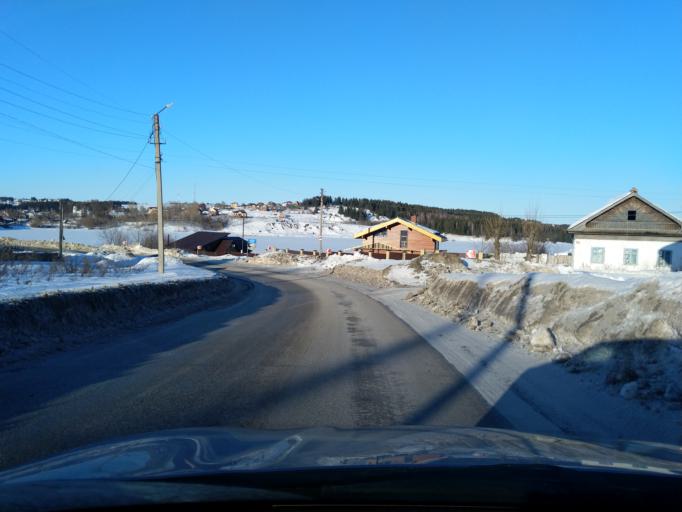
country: RU
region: Perm
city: Polazna
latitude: 58.2993
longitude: 56.4192
